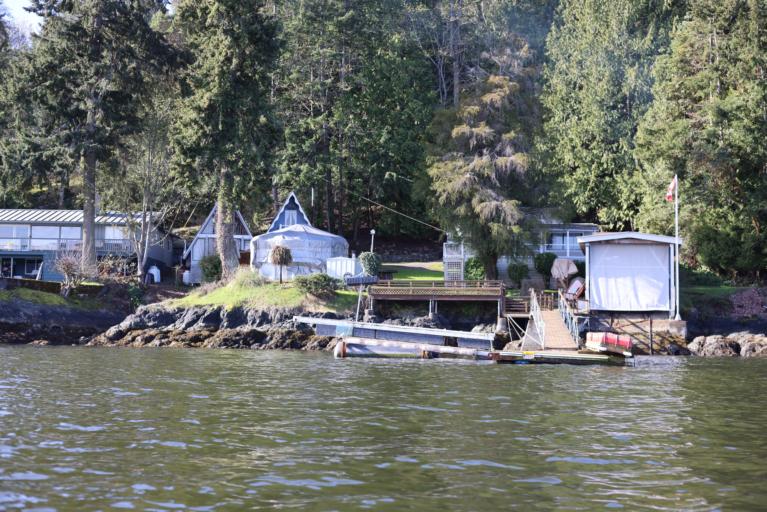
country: CA
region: British Columbia
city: North Saanich
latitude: 48.5760
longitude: -123.4798
